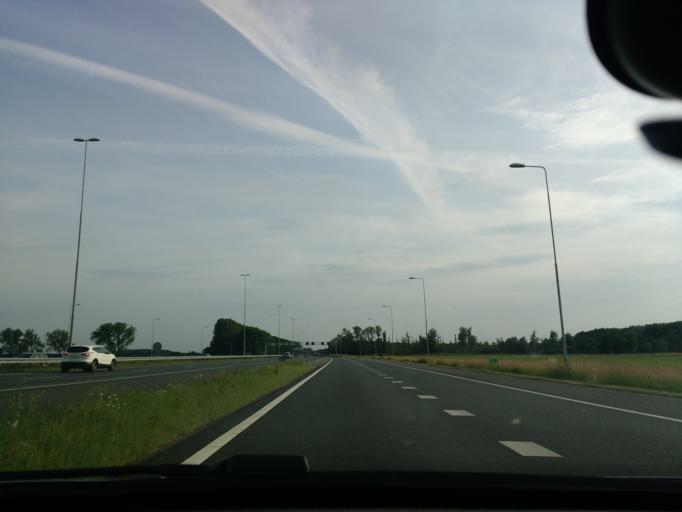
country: NL
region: Gelderland
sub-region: Gemeente Wijchen
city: Bergharen
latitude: 51.8552
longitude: 5.7075
